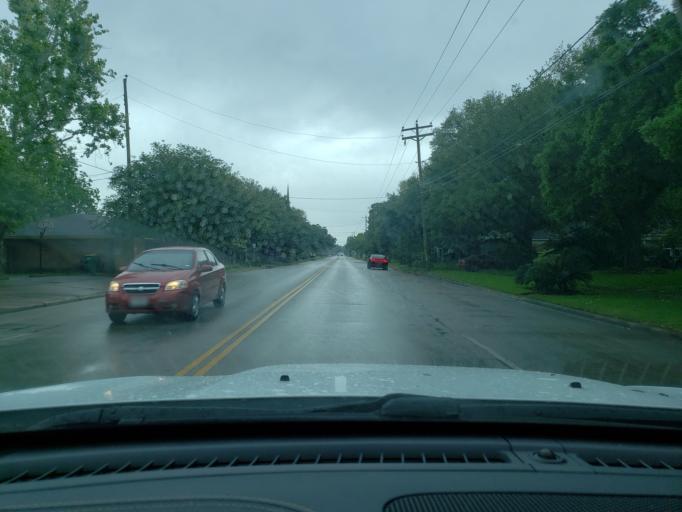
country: US
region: Texas
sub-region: Harris County
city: Baytown
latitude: 29.7376
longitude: -94.9710
